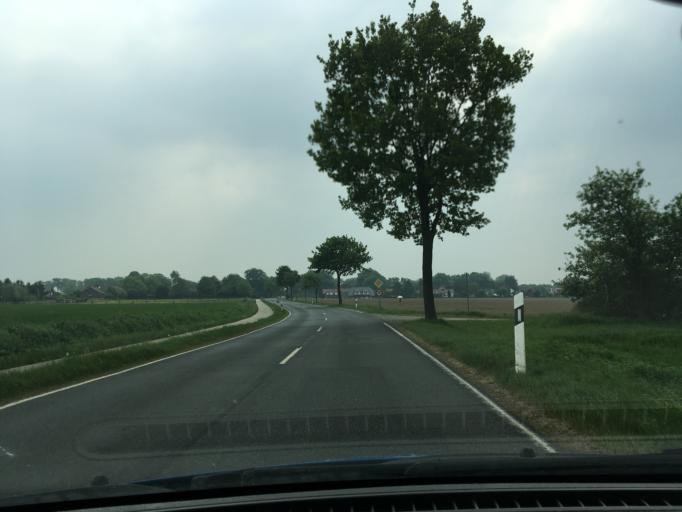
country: DE
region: Lower Saxony
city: Buchholz in der Nordheide
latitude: 53.3881
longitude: 9.8601
